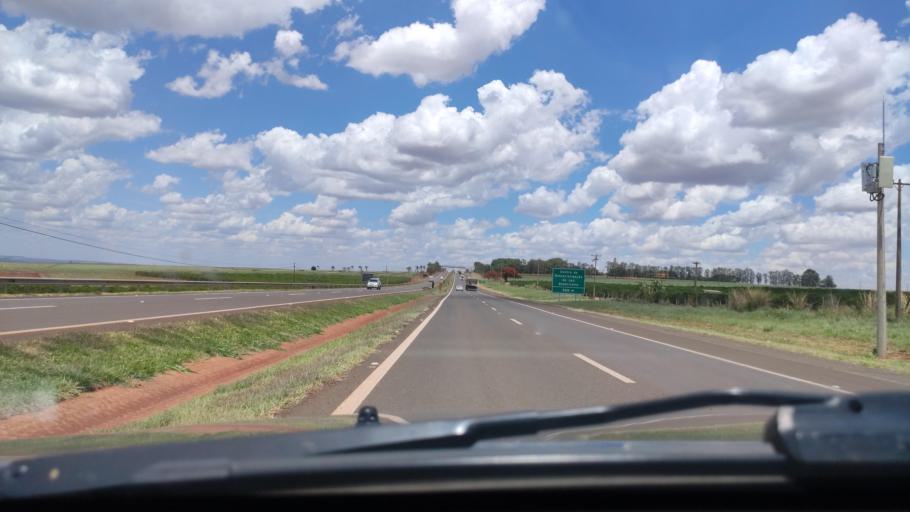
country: BR
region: Sao Paulo
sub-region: Jau
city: Jau
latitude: -22.3047
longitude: -48.6095
